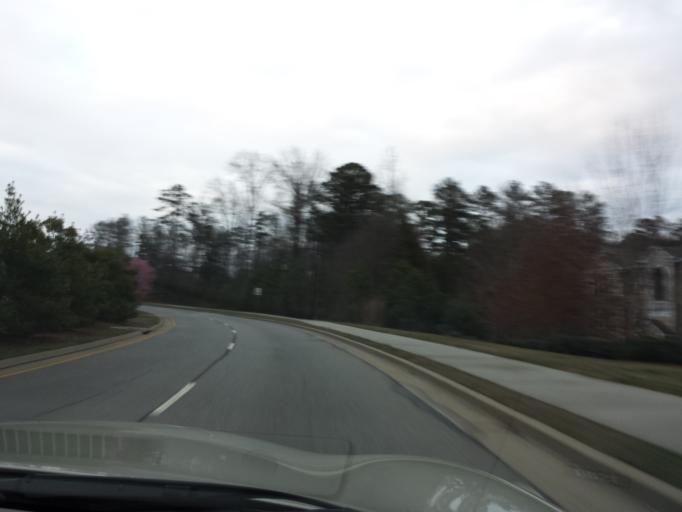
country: US
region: Georgia
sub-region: Fulton County
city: Alpharetta
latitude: 34.0631
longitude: -84.2843
